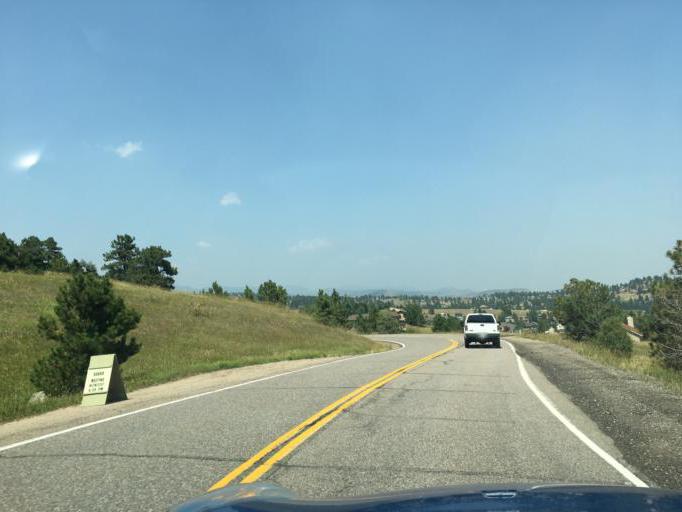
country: US
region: Colorado
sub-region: Jefferson County
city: Genesee
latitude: 39.6975
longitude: -105.2712
